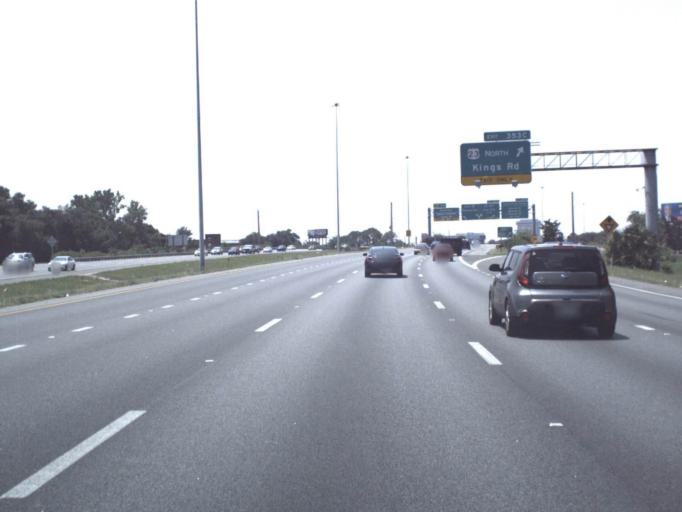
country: US
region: Florida
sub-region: Duval County
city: Jacksonville
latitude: 30.3399
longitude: -81.6683
